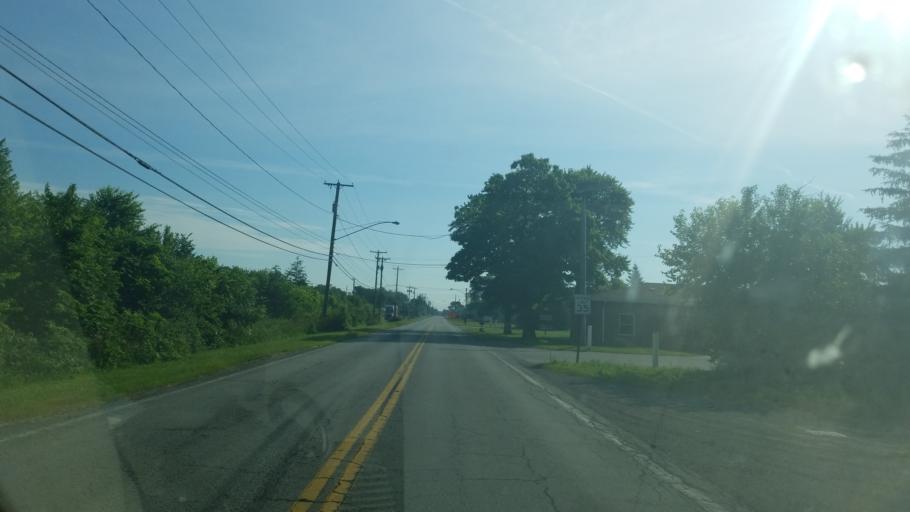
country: US
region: Ohio
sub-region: Hancock County
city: Findlay
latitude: 41.0173
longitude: -83.6764
